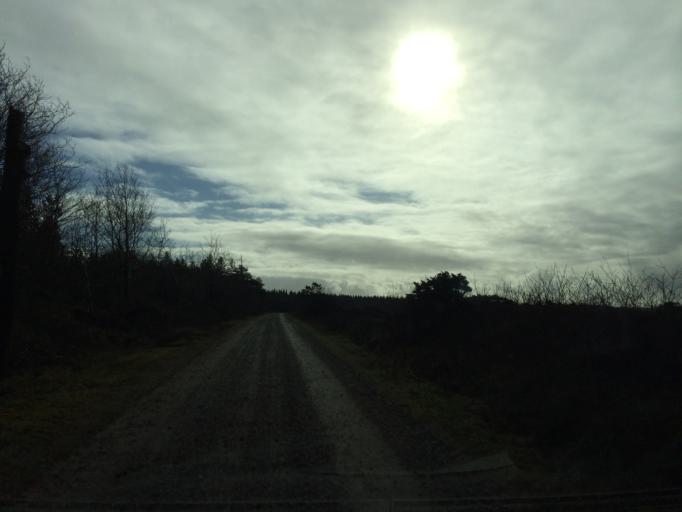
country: DK
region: Central Jutland
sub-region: Holstebro Kommune
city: Ulfborg
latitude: 56.2599
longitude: 8.4244
